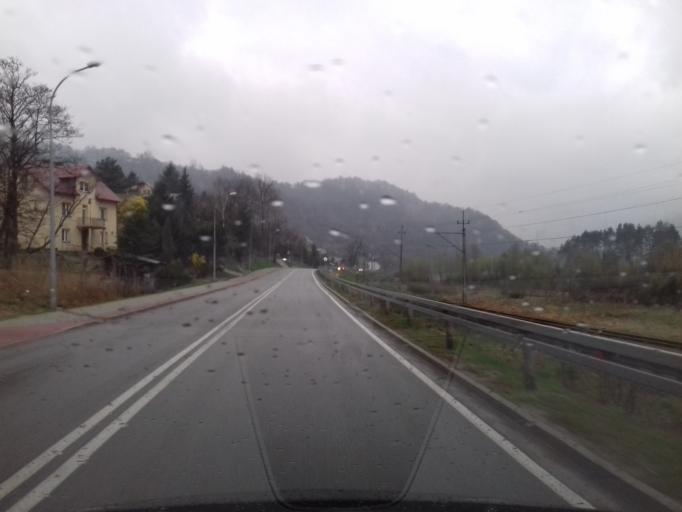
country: PL
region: Lesser Poland Voivodeship
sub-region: Powiat nowosadecki
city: Piwniczna-Zdroj
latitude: 49.4514
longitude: 20.6983
